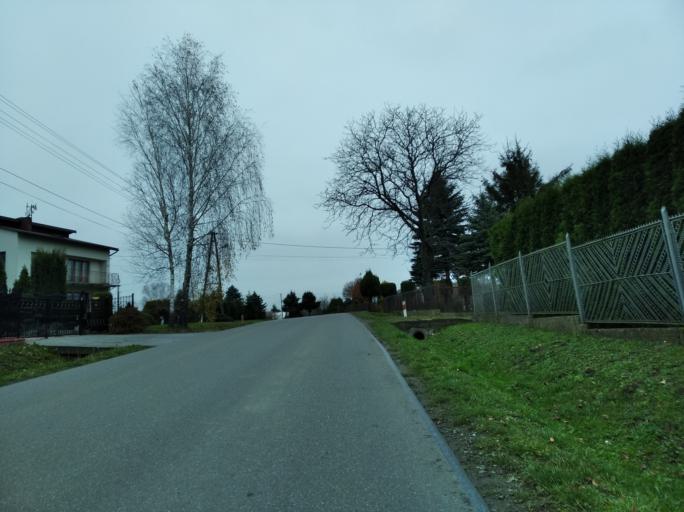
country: PL
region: Subcarpathian Voivodeship
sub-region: Powiat krosnienski
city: Chorkowka
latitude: 49.6728
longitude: 21.6830
